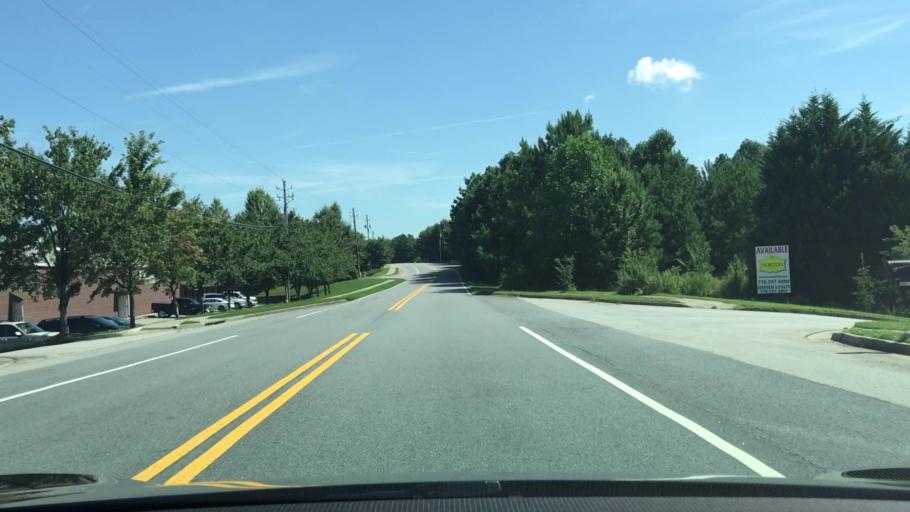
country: US
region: Georgia
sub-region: Gwinnett County
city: Suwanee
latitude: 34.0704
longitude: -84.0594
